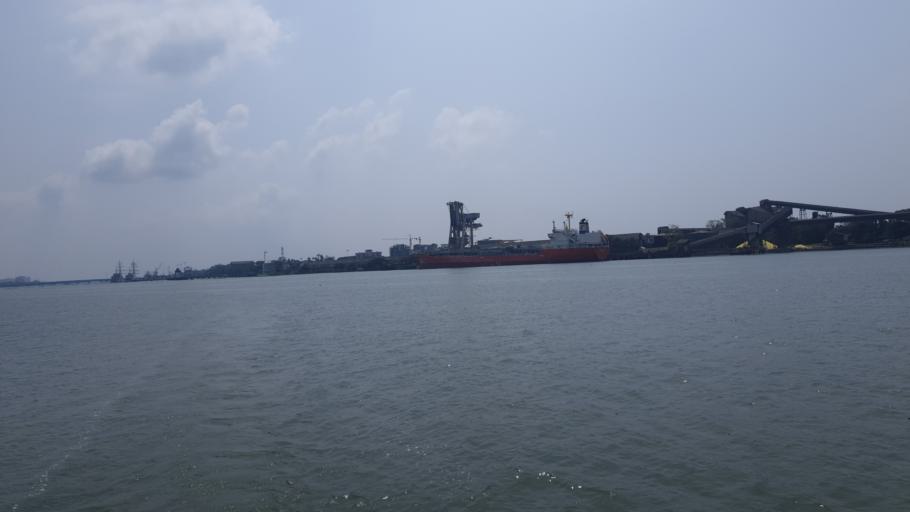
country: IN
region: Kerala
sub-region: Ernakulam
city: Cochin
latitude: 9.9693
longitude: 76.2752
